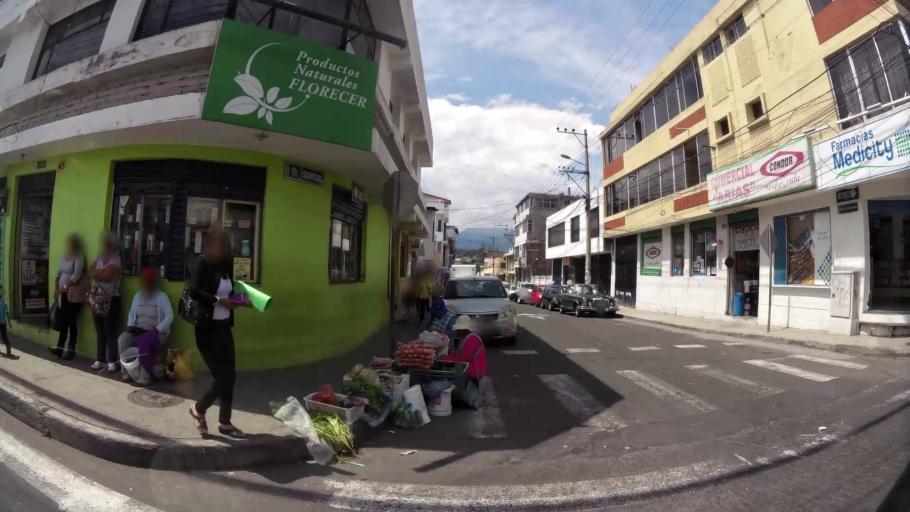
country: EC
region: Pichincha
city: Quito
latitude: -0.2140
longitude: -78.4040
